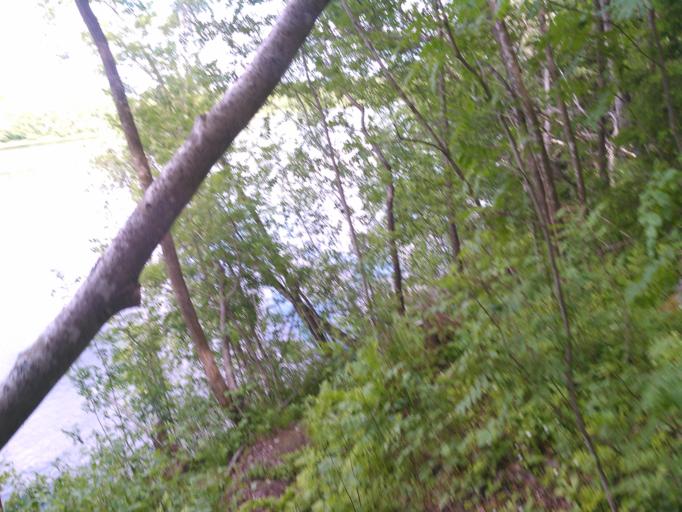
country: SE
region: Vaesterbotten
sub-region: Umea Kommun
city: Roback
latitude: 63.8234
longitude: 20.1979
